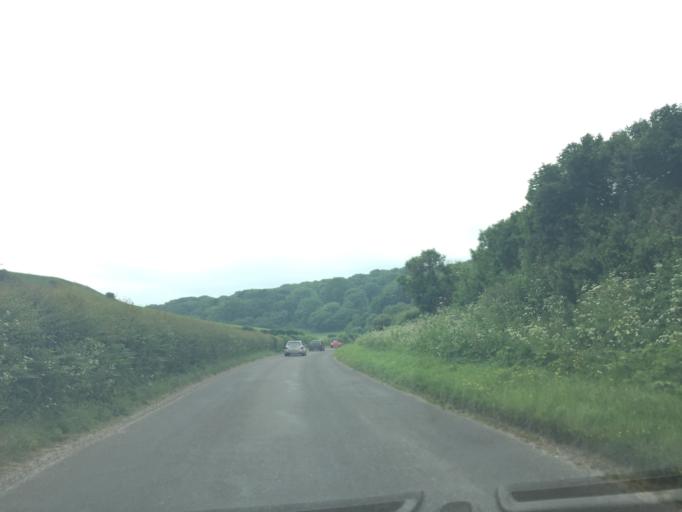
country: GB
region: England
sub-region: Dorset
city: Bovington Camp
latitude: 50.6522
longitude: -2.2720
